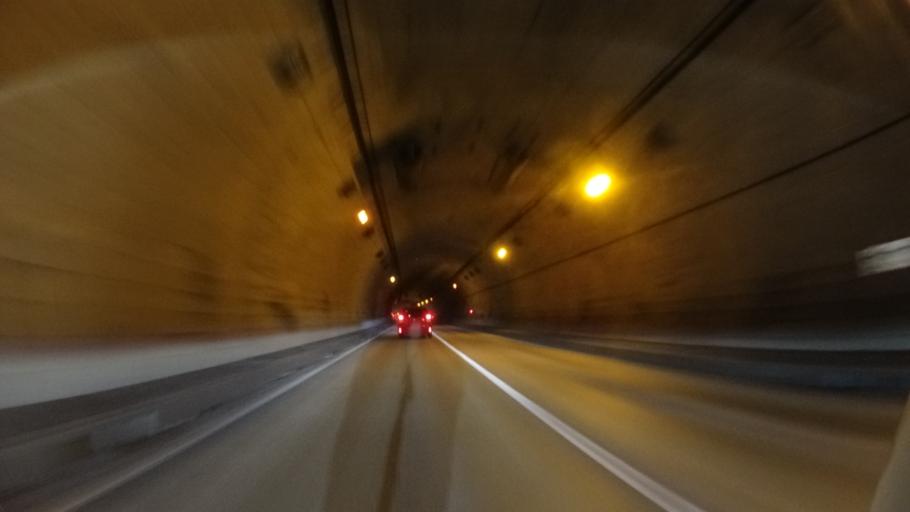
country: JP
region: Fukui
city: Ono
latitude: 35.9911
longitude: 136.4537
